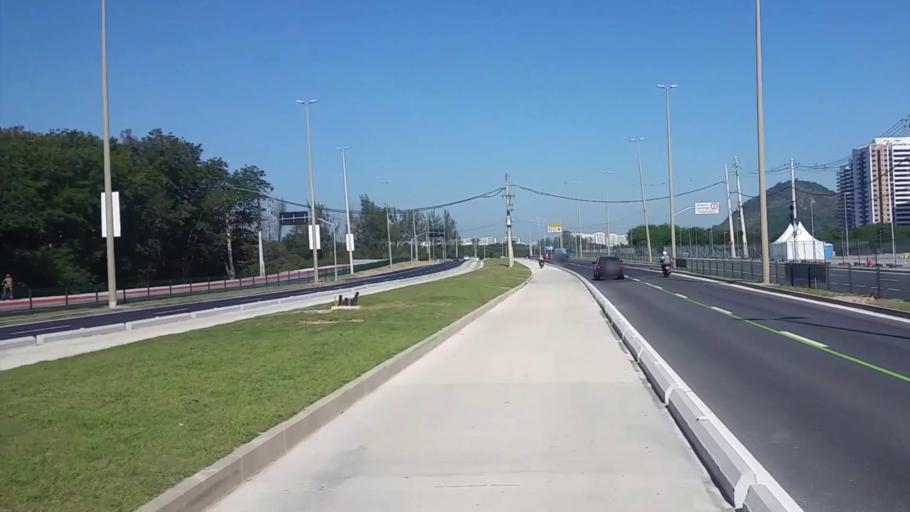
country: BR
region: Rio de Janeiro
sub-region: Nilopolis
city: Nilopolis
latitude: -22.9776
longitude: -43.4071
